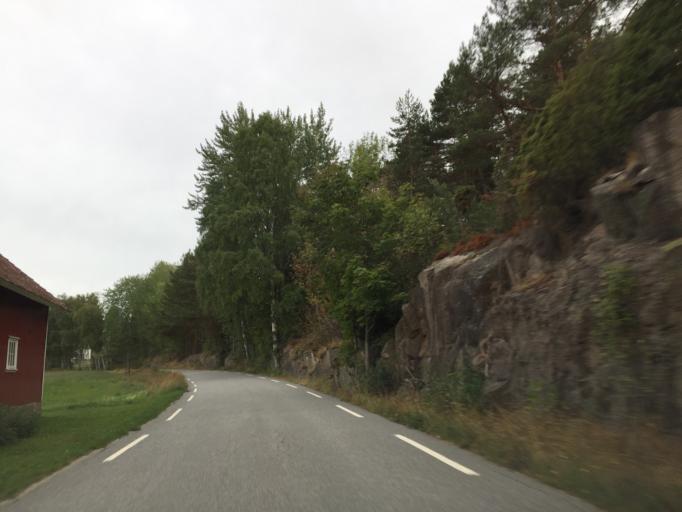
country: NO
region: Ostfold
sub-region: Hvaler
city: Skjaerhalden
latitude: 59.0683
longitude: 11.0052
